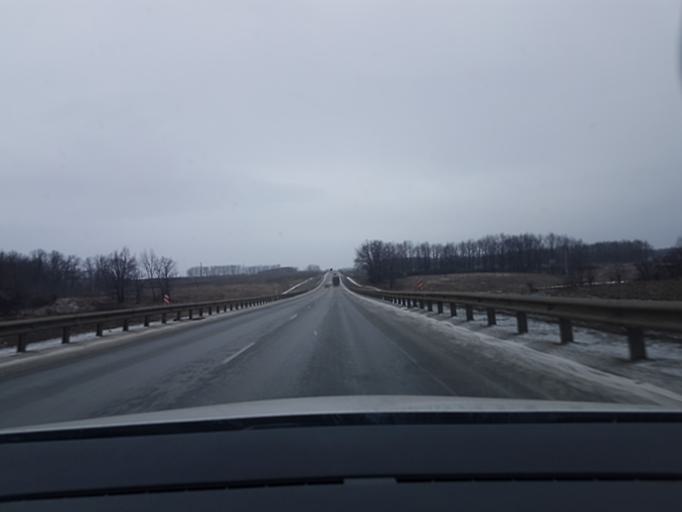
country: RU
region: Tambov
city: Michurinsk
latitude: 52.9958
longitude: 40.5499
